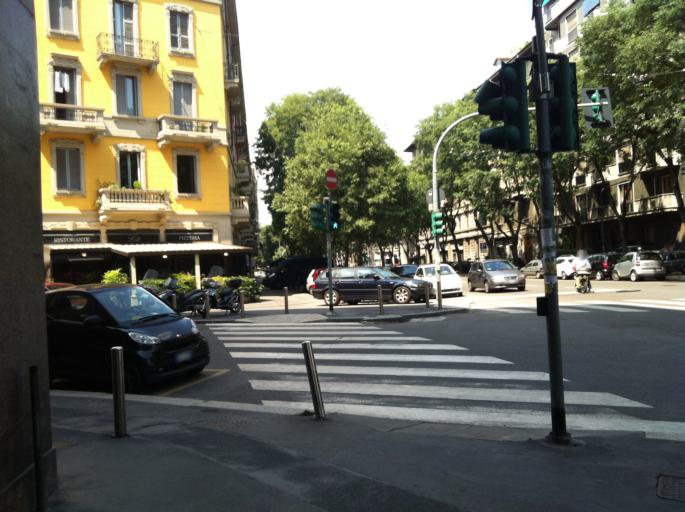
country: IT
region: Lombardy
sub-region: Citta metropolitana di Milano
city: Milano
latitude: 45.4748
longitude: 9.2152
